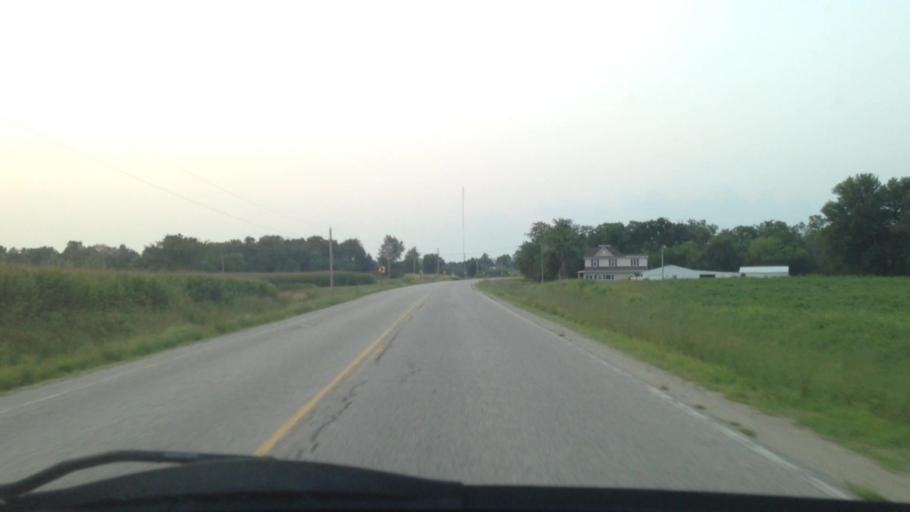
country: US
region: Iowa
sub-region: Benton County
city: Urbana
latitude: 42.1409
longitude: -91.8777
